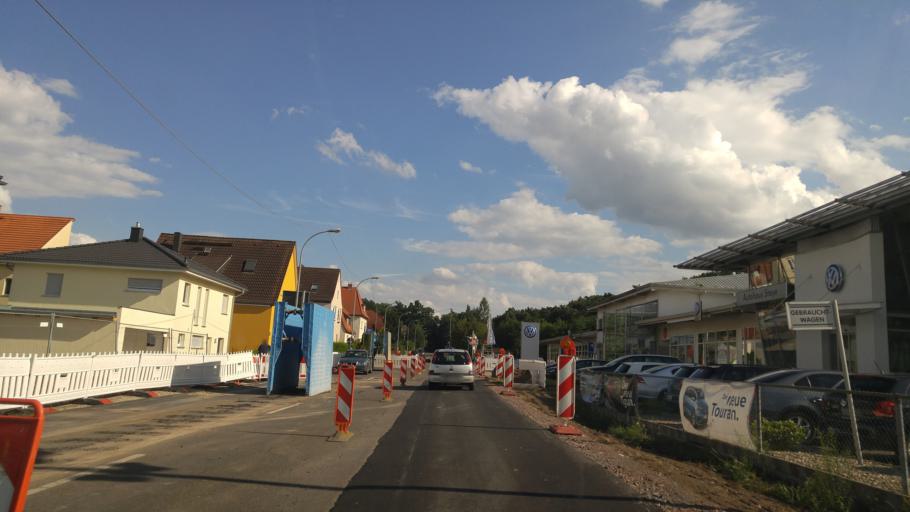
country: DE
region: Saxony-Anhalt
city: Lieskau
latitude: 51.5070
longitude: 11.8830
